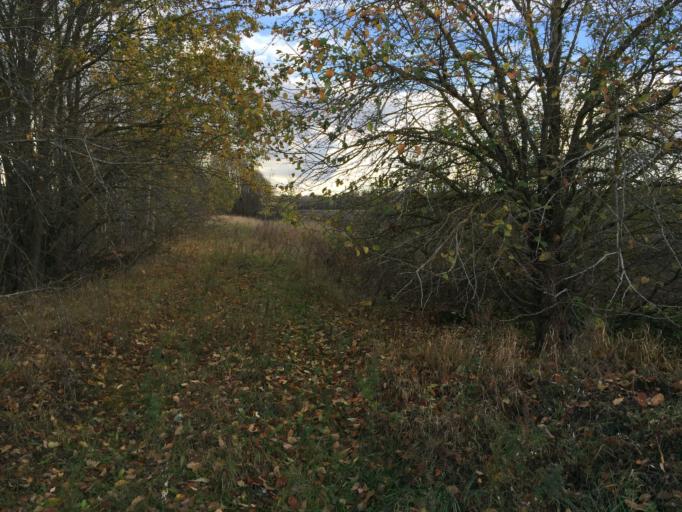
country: LV
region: Tukuma Rajons
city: Tukums
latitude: 56.9635
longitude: 23.0325
